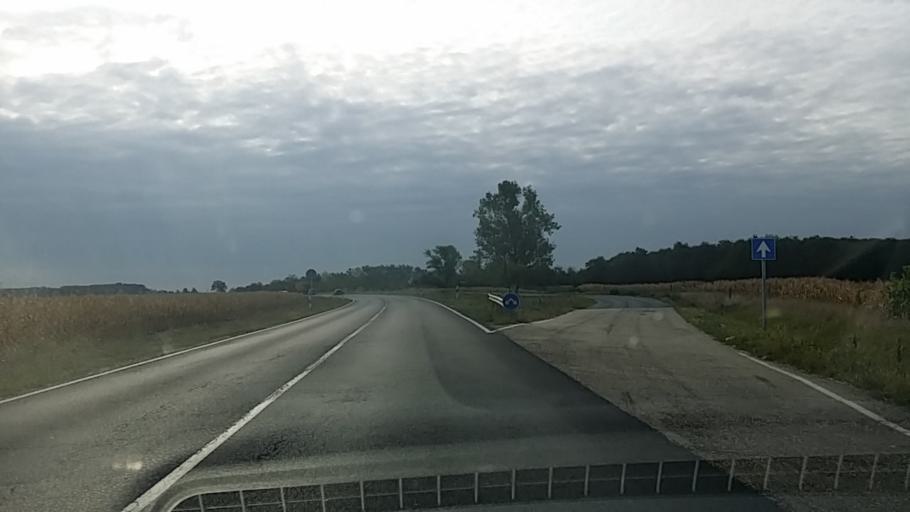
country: HU
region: Gyor-Moson-Sopron
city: Fertoszentmiklos
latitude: 47.5935
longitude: 16.9374
